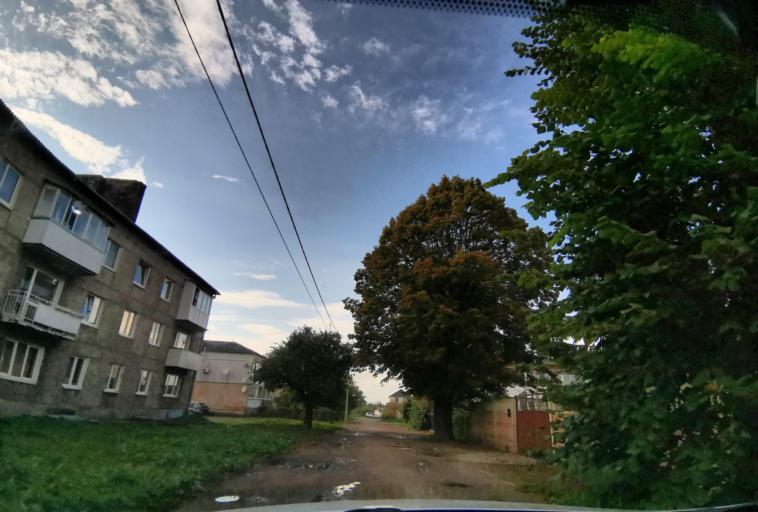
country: RU
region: Kaliningrad
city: Chernyakhovsk
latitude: 54.6571
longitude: 21.8363
